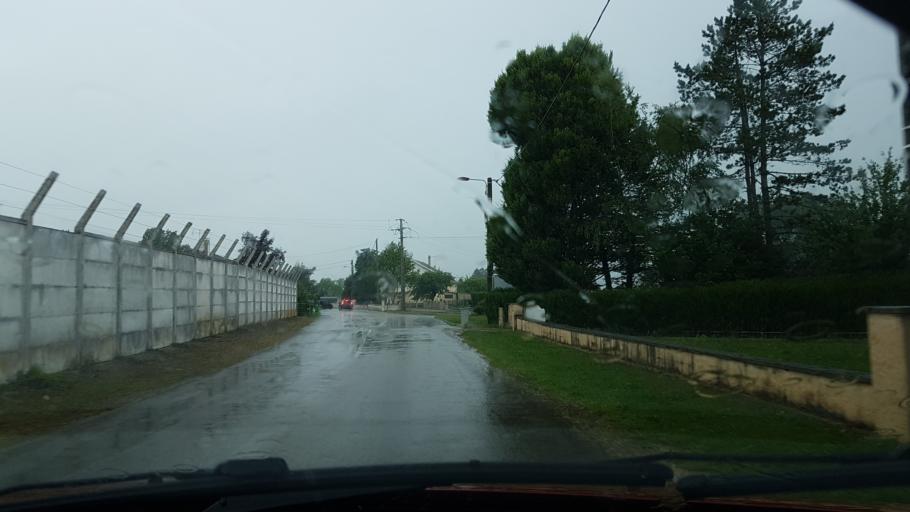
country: FR
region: Franche-Comte
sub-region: Departement du Jura
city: Clairvaux-les-Lacs
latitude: 46.5797
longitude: 5.6936
